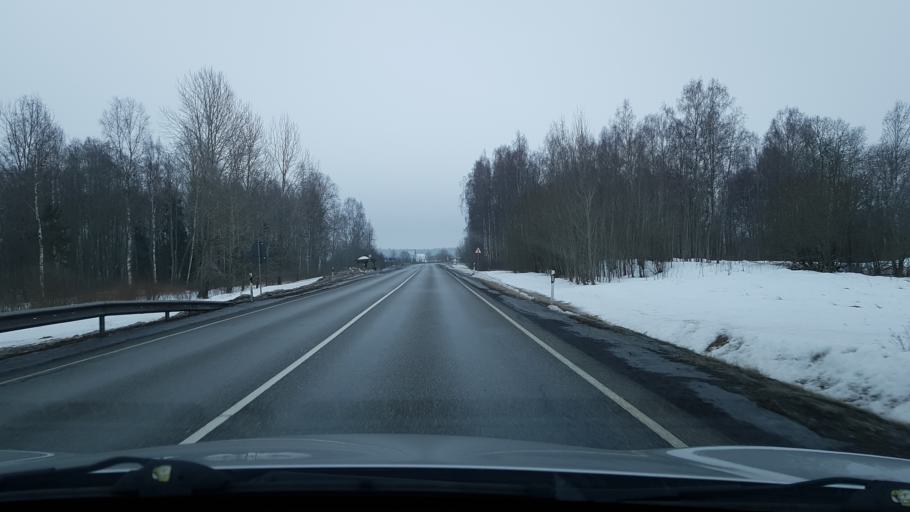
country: EE
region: Valgamaa
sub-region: Valga linn
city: Valga
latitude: 57.9119
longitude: 26.1821
